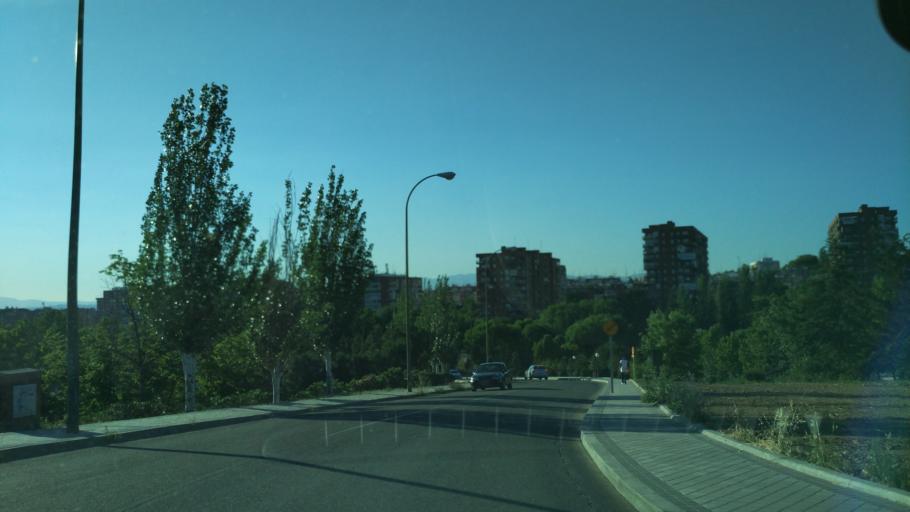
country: ES
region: Madrid
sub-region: Provincia de Madrid
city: Tetuan de las Victorias
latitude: 40.4688
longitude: -3.7099
